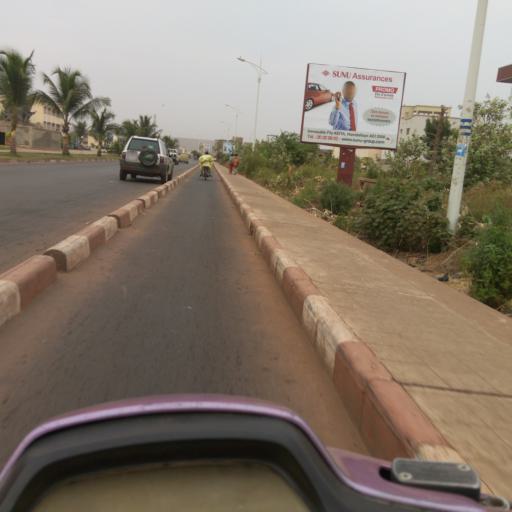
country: ML
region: Bamako
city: Bamako
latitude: 12.6546
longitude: -7.9317
